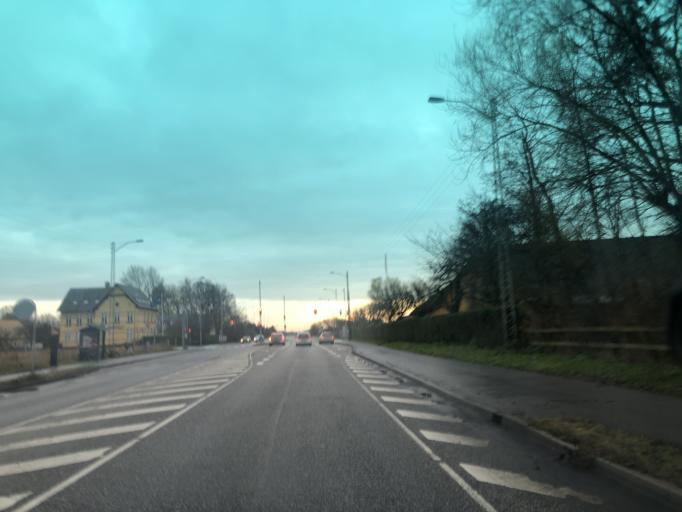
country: DK
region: Capital Region
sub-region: Tarnby Kommune
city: Tarnby
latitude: 55.6101
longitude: 12.6144
